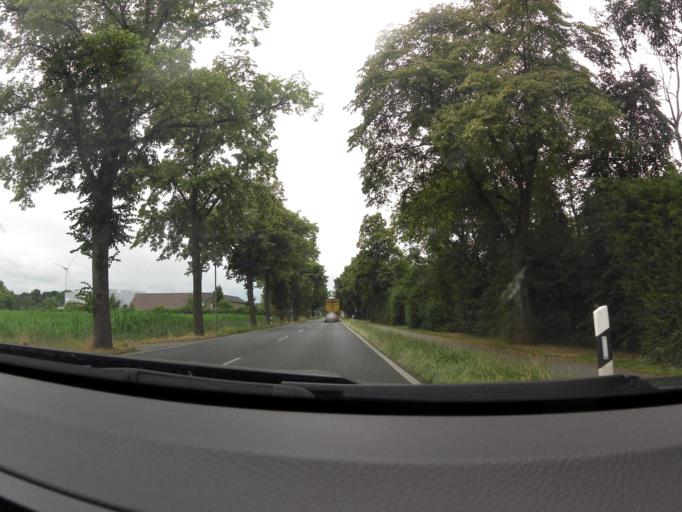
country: DE
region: North Rhine-Westphalia
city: Geldern
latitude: 51.4924
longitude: 6.2992
